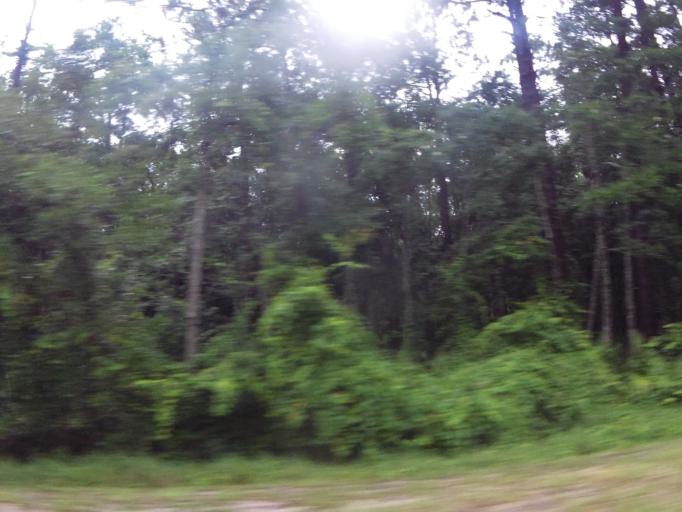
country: US
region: Florida
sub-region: Duval County
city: Jacksonville Beach
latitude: 30.2678
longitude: -81.5013
